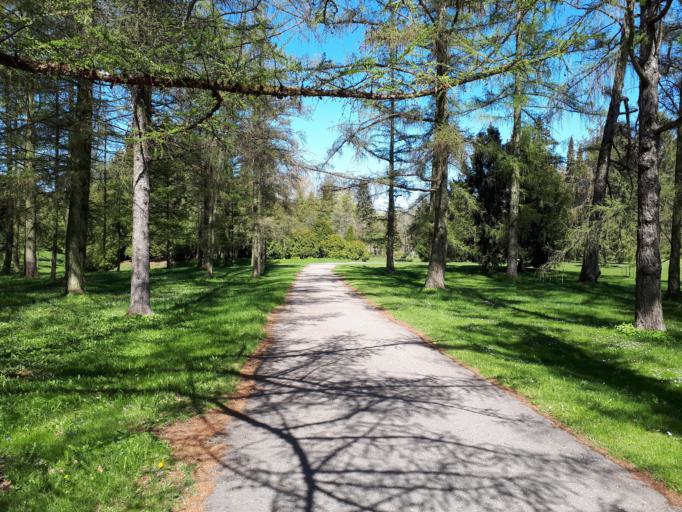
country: LT
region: Kauno apskritis
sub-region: Kaunas
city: Aleksotas
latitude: 54.8690
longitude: 23.9070
